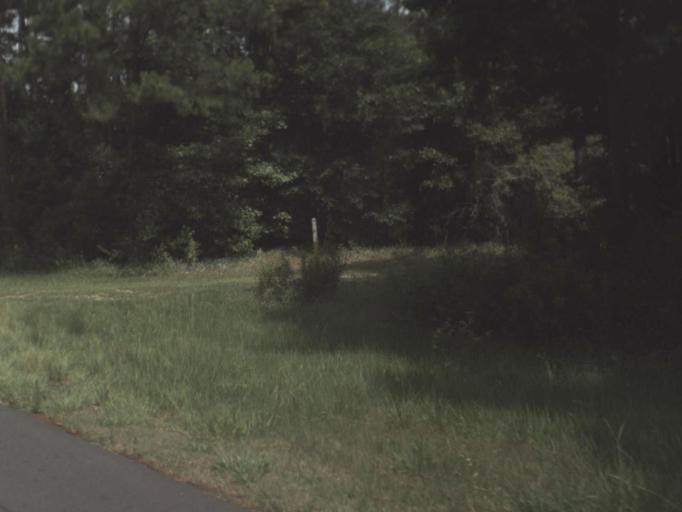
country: US
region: Florida
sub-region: Jefferson County
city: Monticello
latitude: 30.4822
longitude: -83.6813
